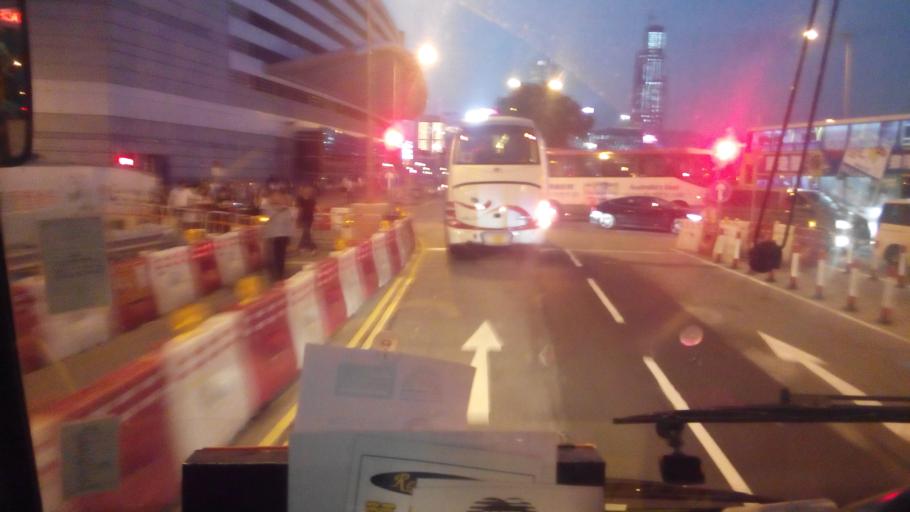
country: HK
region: Wanchai
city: Wan Chai
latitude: 22.2824
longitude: 114.1746
